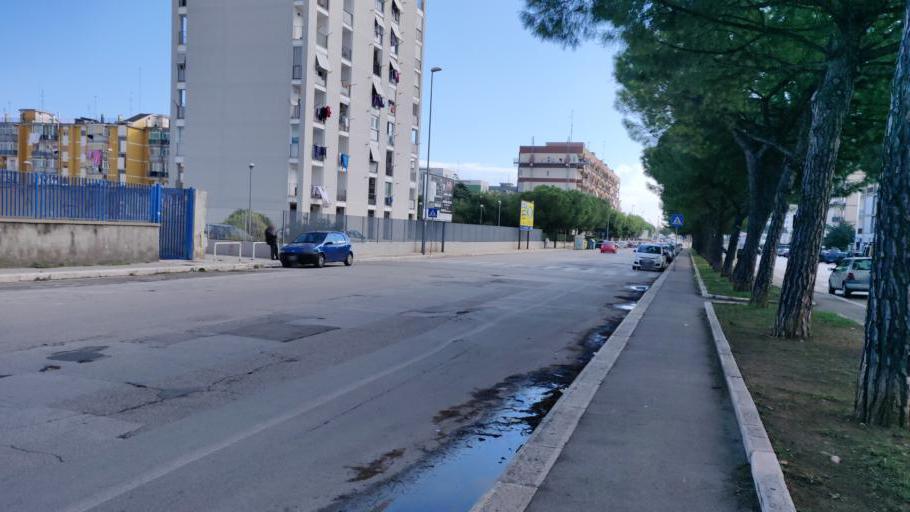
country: IT
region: Apulia
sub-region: Provincia di Bari
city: Bari
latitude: 41.1076
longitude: 16.8964
